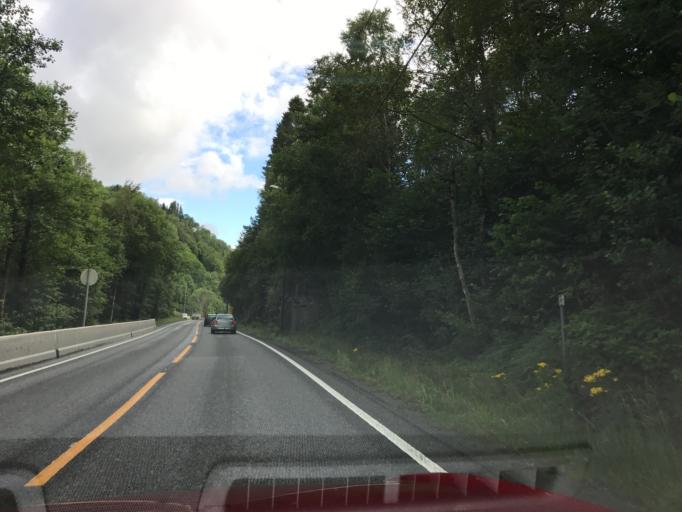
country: NO
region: Hordaland
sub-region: Os
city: Osoyro
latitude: 60.1737
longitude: 5.4482
